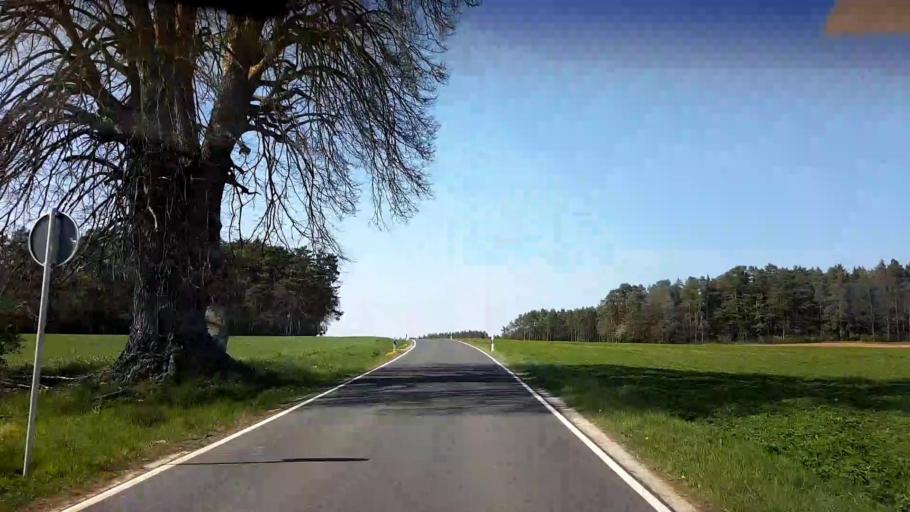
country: DE
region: Bavaria
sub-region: Upper Franconia
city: Pottenstein
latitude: 49.8019
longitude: 11.3739
